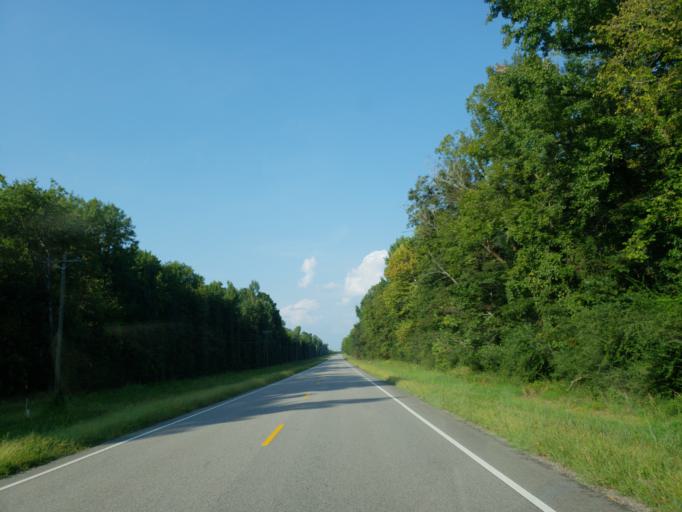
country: US
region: Alabama
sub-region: Greene County
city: Eutaw
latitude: 32.7373
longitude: -88.0541
